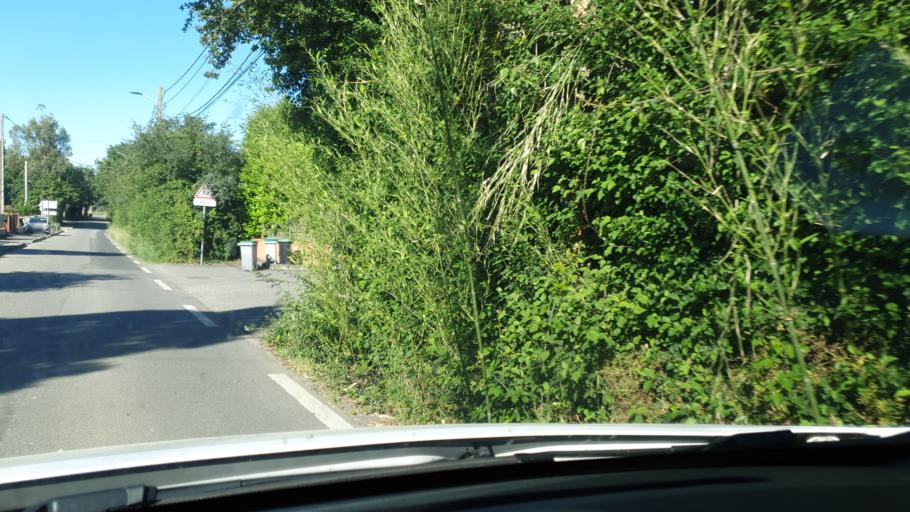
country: FR
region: Midi-Pyrenees
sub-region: Departement de la Haute-Garonne
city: Saint-Orens-de-Gameville
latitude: 43.5582
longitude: 1.5072
